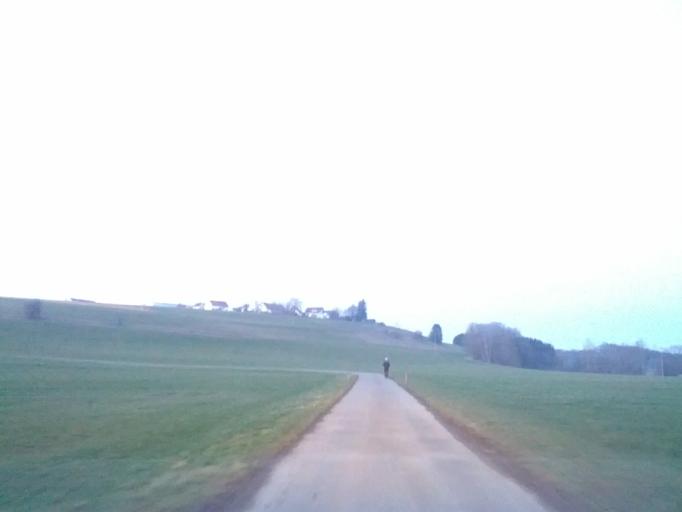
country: DE
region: Baden-Wuerttemberg
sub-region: Tuebingen Region
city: Steinhausen an der Rottum
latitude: 47.9797
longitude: 9.9877
